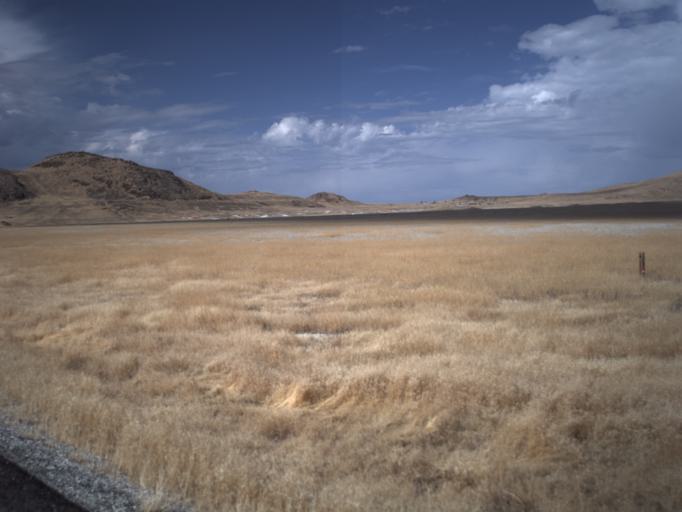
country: US
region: Utah
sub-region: Tooele County
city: Wendover
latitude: 41.3862
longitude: -113.9828
